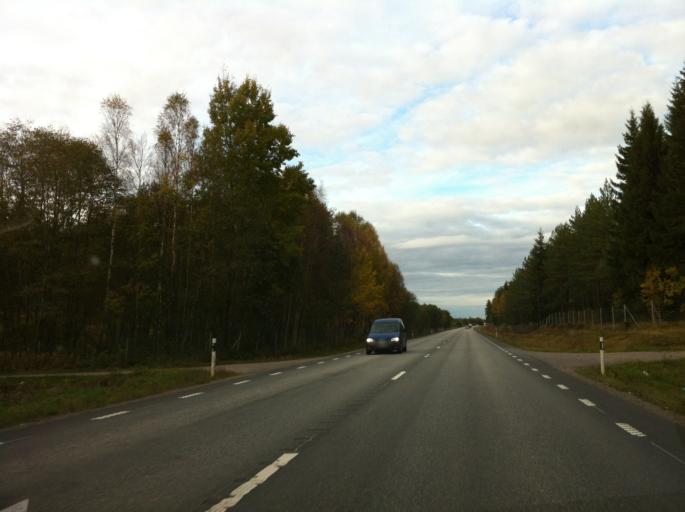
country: SE
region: OErebro
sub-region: Askersunds Kommun
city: Asbro
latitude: 58.9573
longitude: 15.0333
